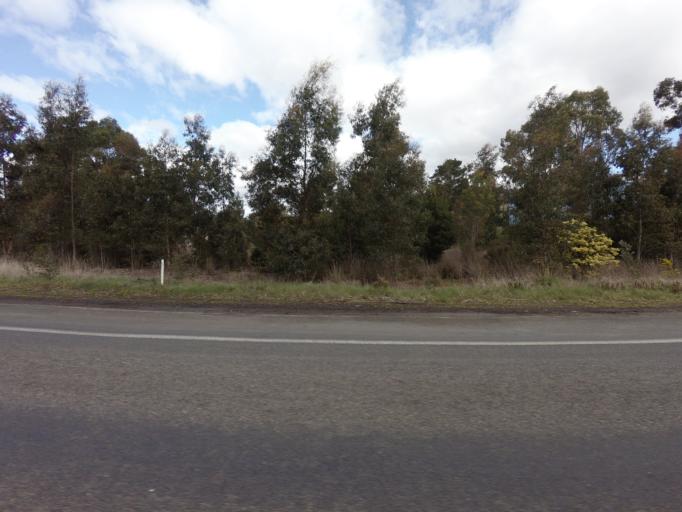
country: AU
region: Tasmania
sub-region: Huon Valley
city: Geeveston
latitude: -43.1559
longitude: 146.9578
